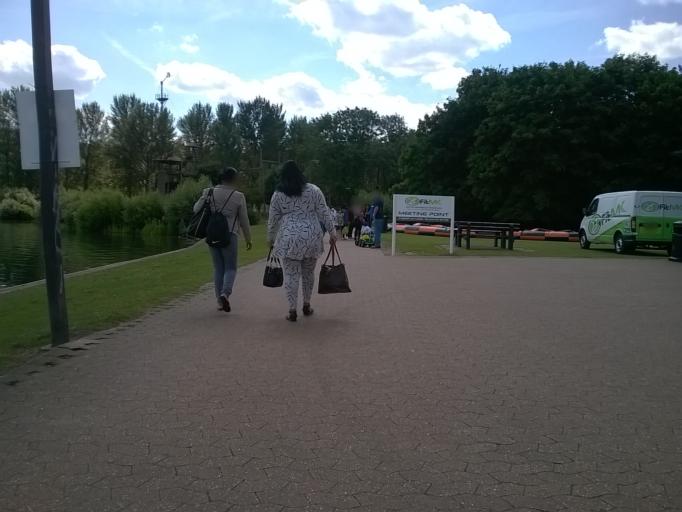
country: GB
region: England
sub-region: Milton Keynes
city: Broughton
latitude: 52.0483
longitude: -0.7218
